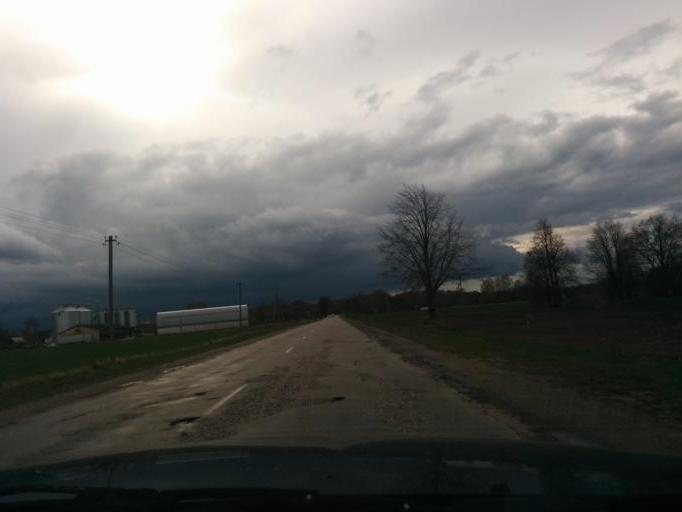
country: LT
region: Siauliu apskritis
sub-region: Joniskis
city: Joniskis
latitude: 56.4182
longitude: 23.5742
